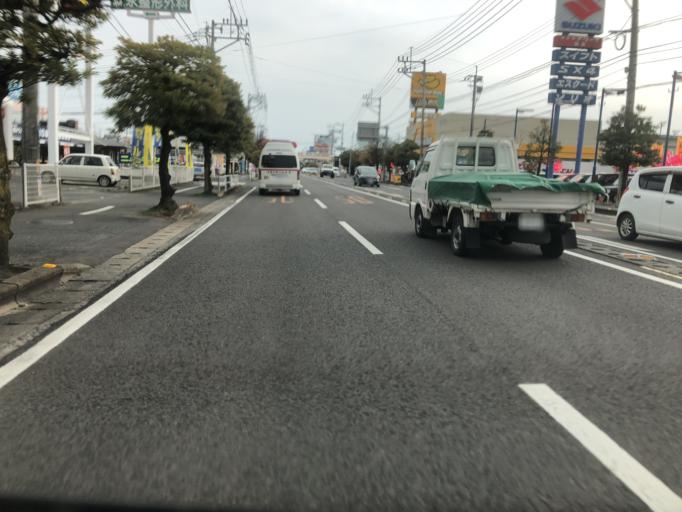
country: JP
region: Saga Prefecture
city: Saga-shi
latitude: 33.2703
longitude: 130.2714
